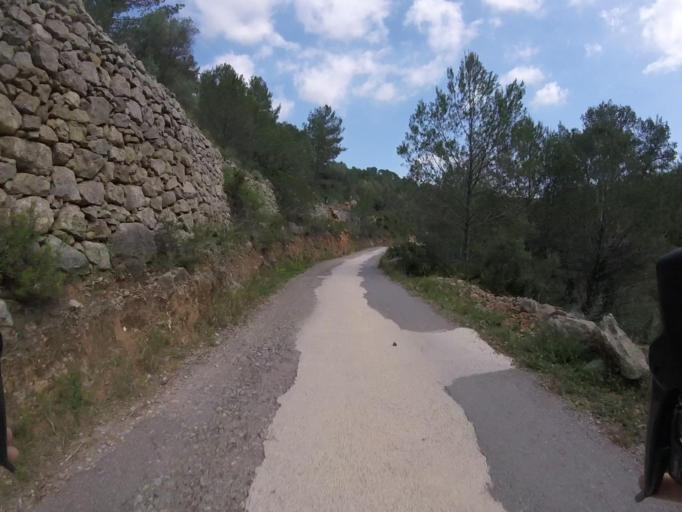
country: ES
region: Valencia
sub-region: Provincia de Castello
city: Cabanes
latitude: 40.1106
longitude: 0.0432
